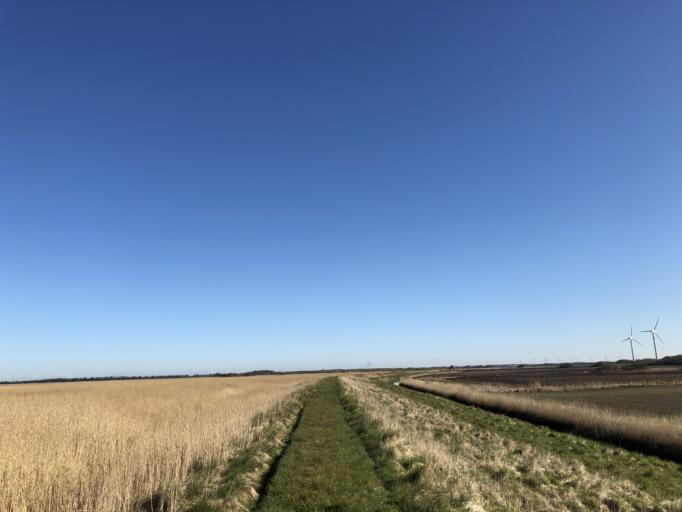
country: DK
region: Central Jutland
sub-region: Holstebro Kommune
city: Ulfborg
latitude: 56.3052
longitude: 8.2918
